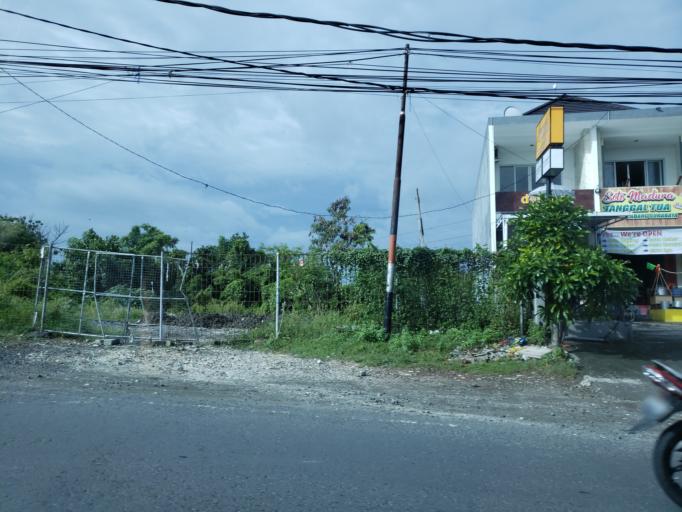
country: ID
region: Bali
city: Karyadharma
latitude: -8.6806
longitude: 115.1883
